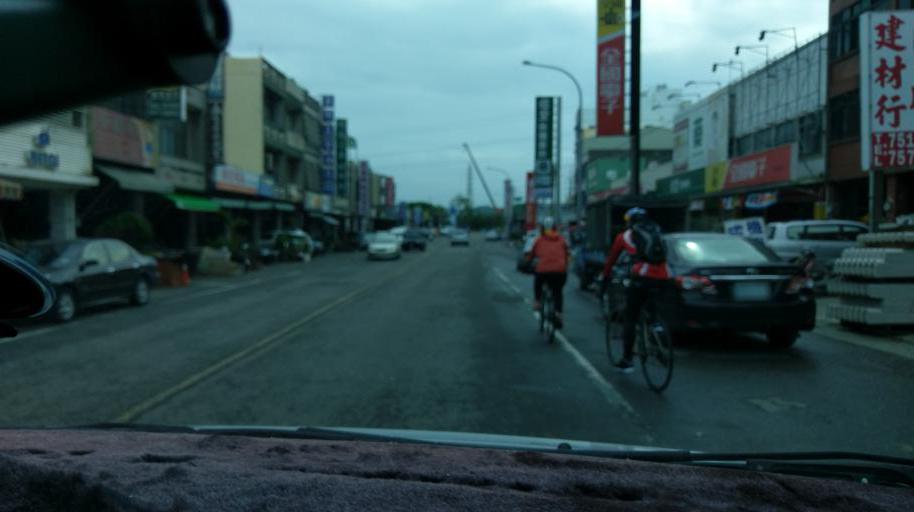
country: TW
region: Taiwan
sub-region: Miaoli
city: Miaoli
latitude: 24.4869
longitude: 120.6778
